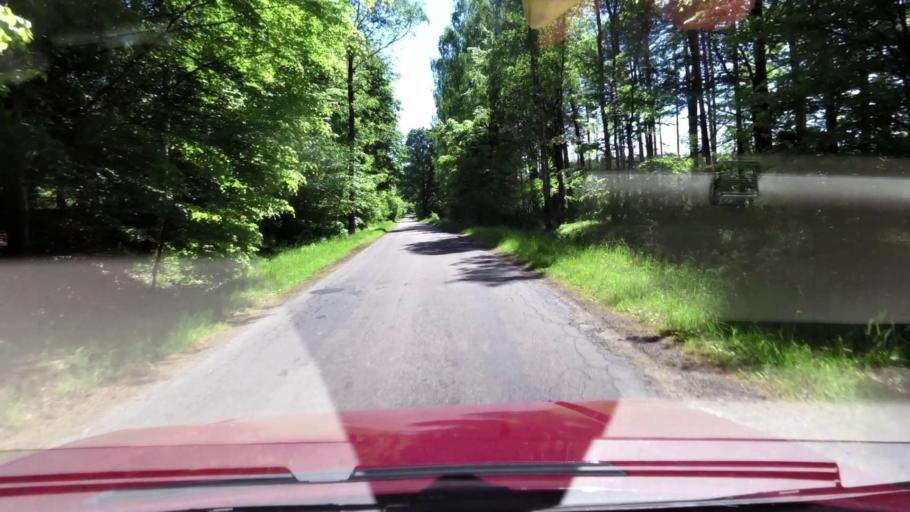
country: PL
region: West Pomeranian Voivodeship
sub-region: Powiat koszalinski
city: Bobolice
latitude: 54.0729
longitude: 16.4992
